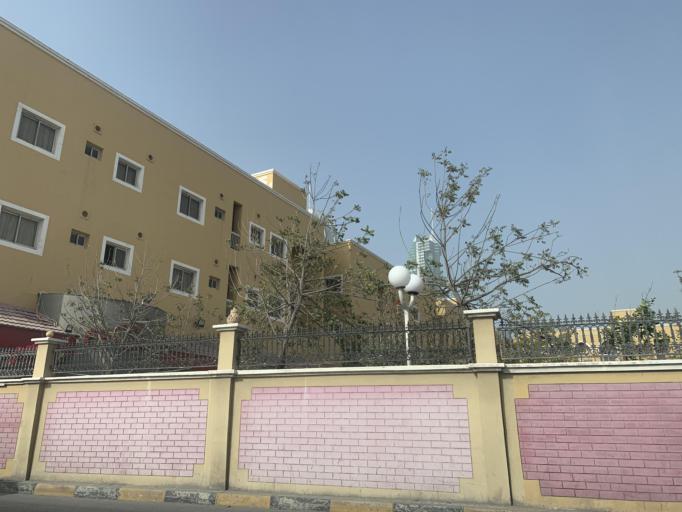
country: BH
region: Manama
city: Manama
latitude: 26.2332
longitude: 50.5707
